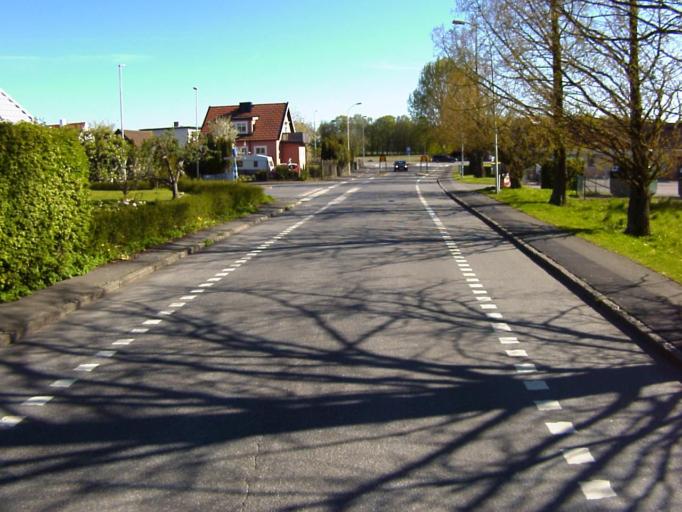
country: SE
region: Skane
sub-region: Kristianstads Kommun
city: Kristianstad
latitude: 56.0297
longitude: 14.1984
